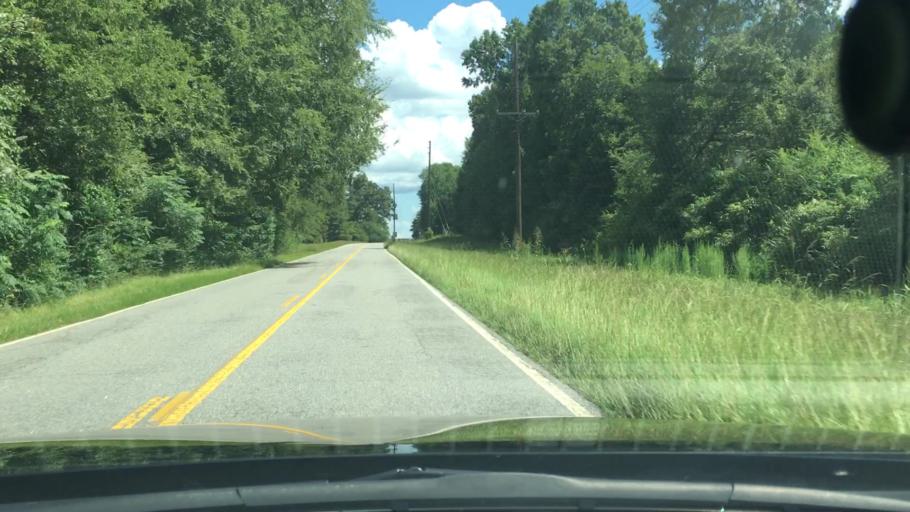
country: US
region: Georgia
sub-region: Putnam County
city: Jefferson
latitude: 33.3792
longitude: -83.2516
